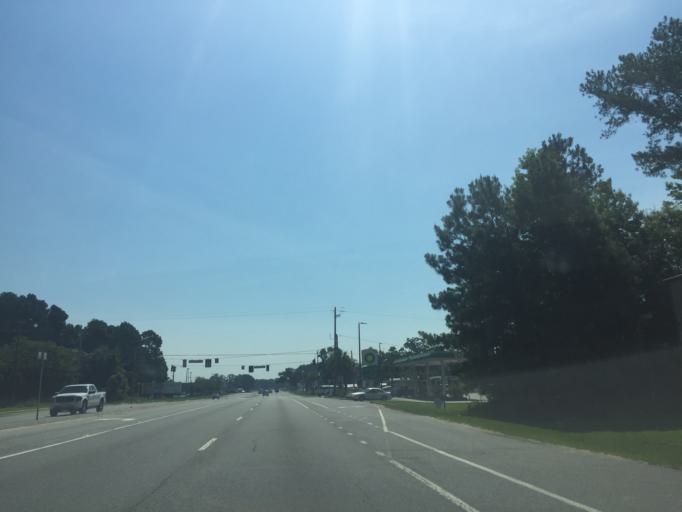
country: US
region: Georgia
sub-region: Chatham County
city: Georgetown
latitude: 31.9971
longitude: -81.2609
